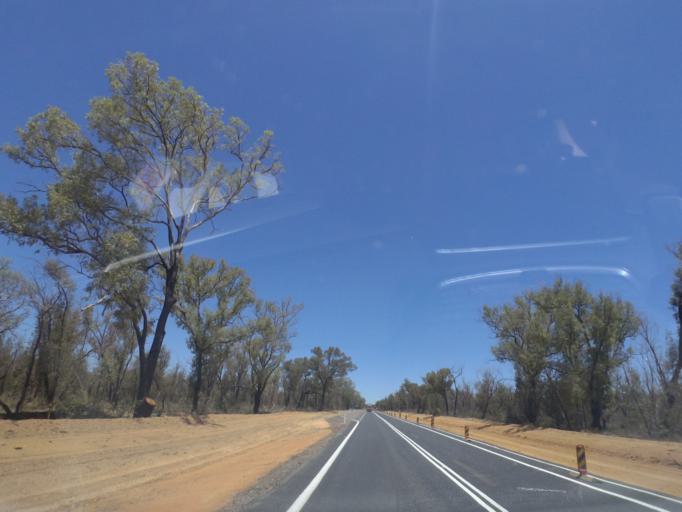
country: AU
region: New South Wales
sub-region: Warrumbungle Shire
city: Coonabarabran
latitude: -30.9350
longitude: 149.4267
